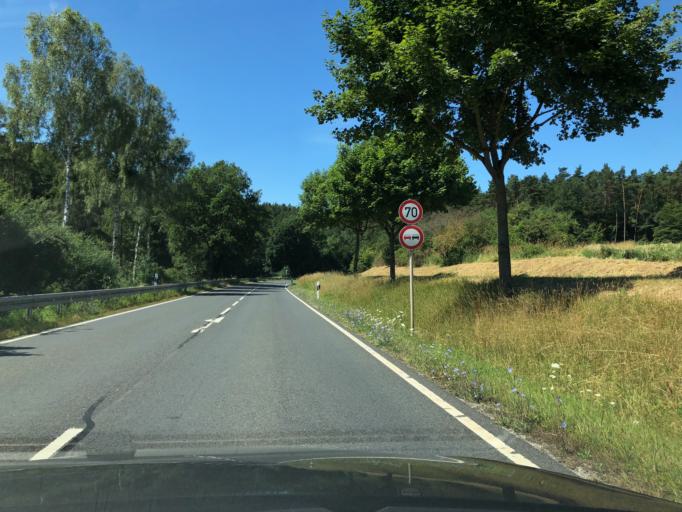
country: DE
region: Bavaria
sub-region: Upper Franconia
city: Niederfullbach
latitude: 50.2198
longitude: 11.0276
